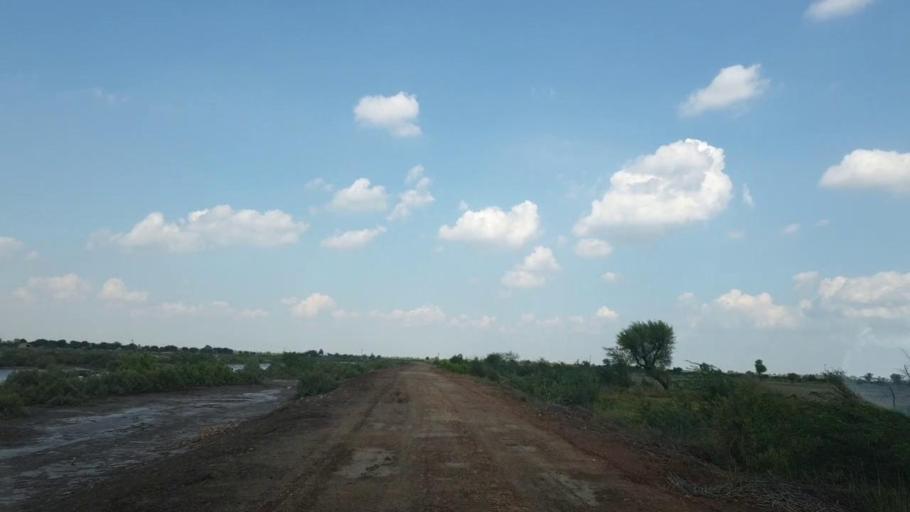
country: PK
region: Sindh
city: Pithoro
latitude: 25.6029
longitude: 69.3745
